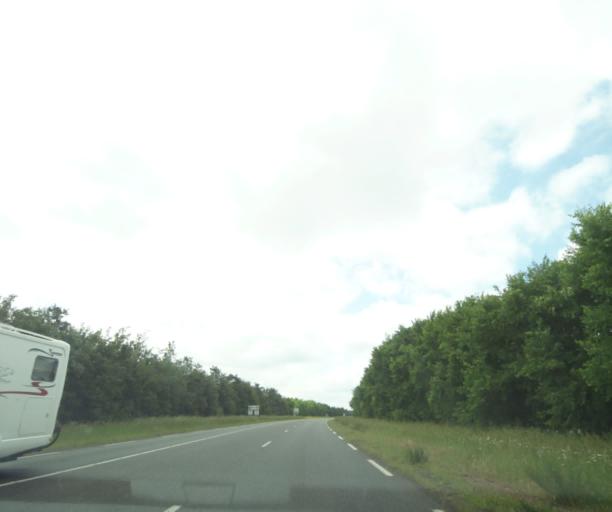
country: FR
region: Poitou-Charentes
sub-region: Departement des Deux-Sevres
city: Airvault
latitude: 46.8198
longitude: -0.2050
